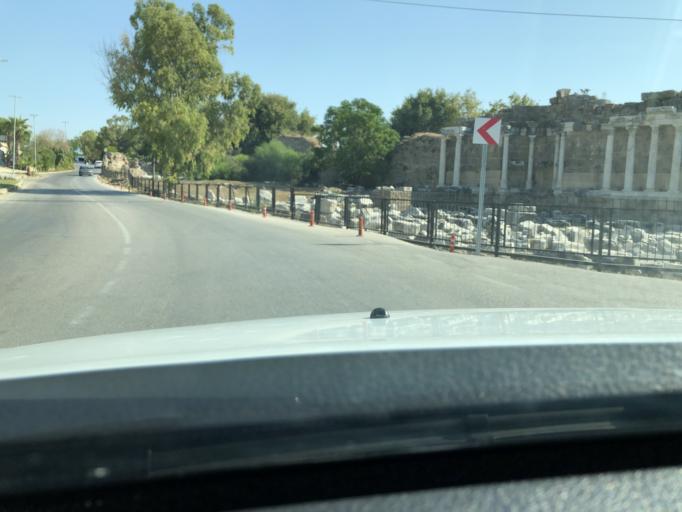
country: TR
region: Antalya
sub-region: Manavgat
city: Side
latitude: 36.7710
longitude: 31.3944
